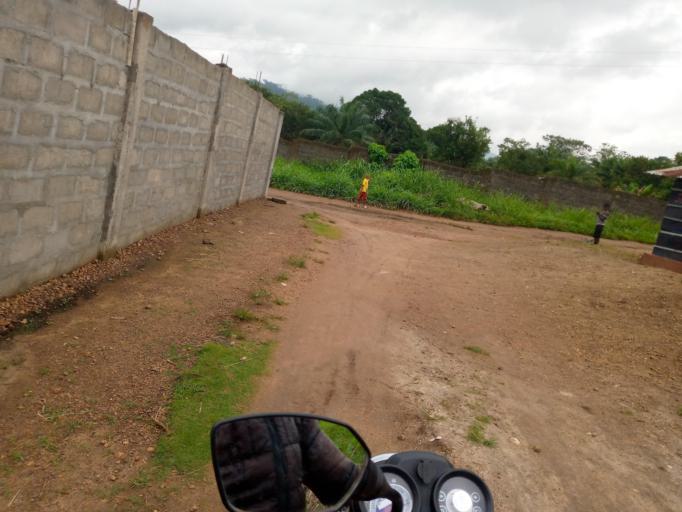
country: SL
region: Eastern Province
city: Kenema
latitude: 7.8485
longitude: -11.2073
